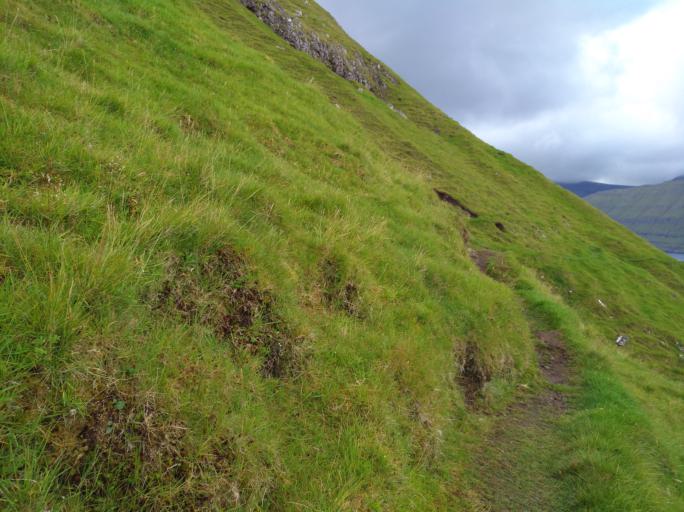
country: FO
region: Eysturoy
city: Fuglafjordur
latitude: 62.2881
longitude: -6.8790
